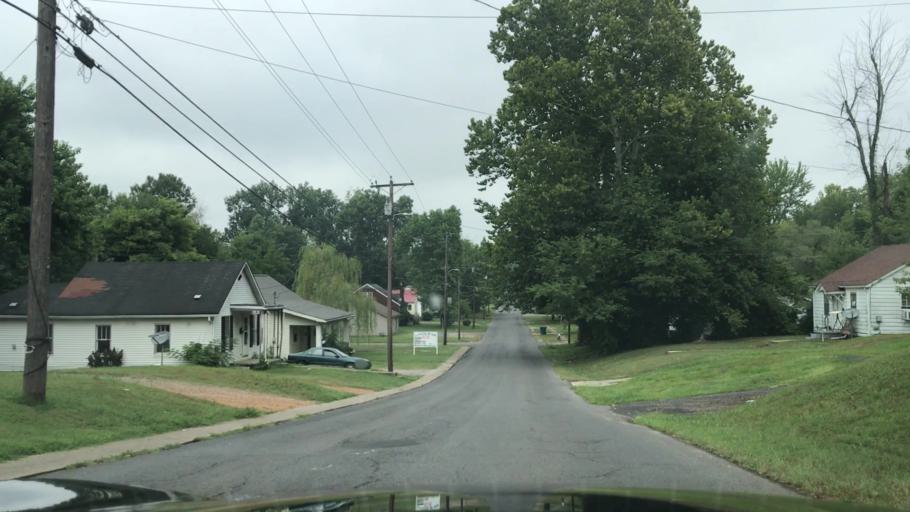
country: US
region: Kentucky
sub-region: Graves County
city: Mayfield
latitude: 36.7326
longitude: -88.6410
